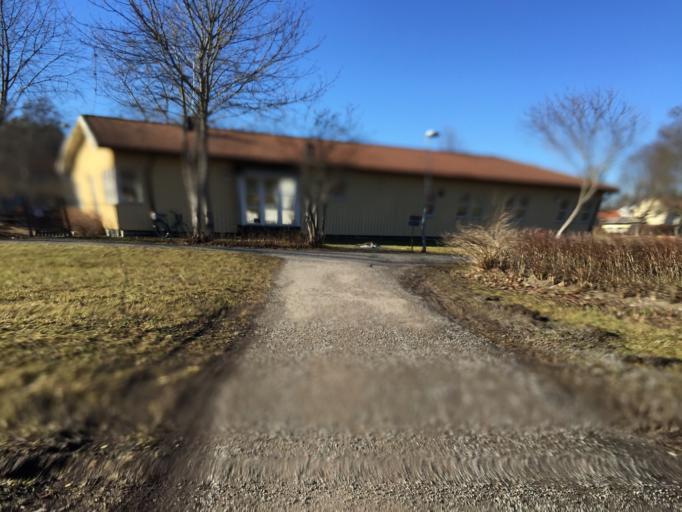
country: SE
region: Stockholm
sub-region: Stockholms Kommun
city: Bromma
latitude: 59.3611
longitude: 17.8896
